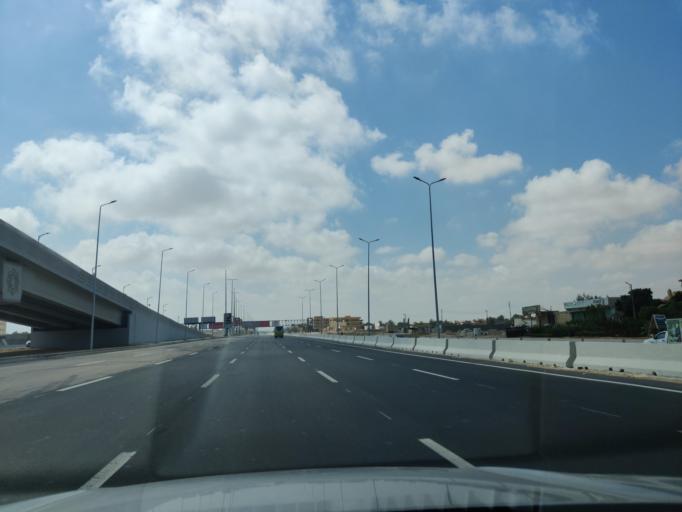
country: EG
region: Muhafazat Matruh
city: Al `Alamayn
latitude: 30.9504
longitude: 28.7723
